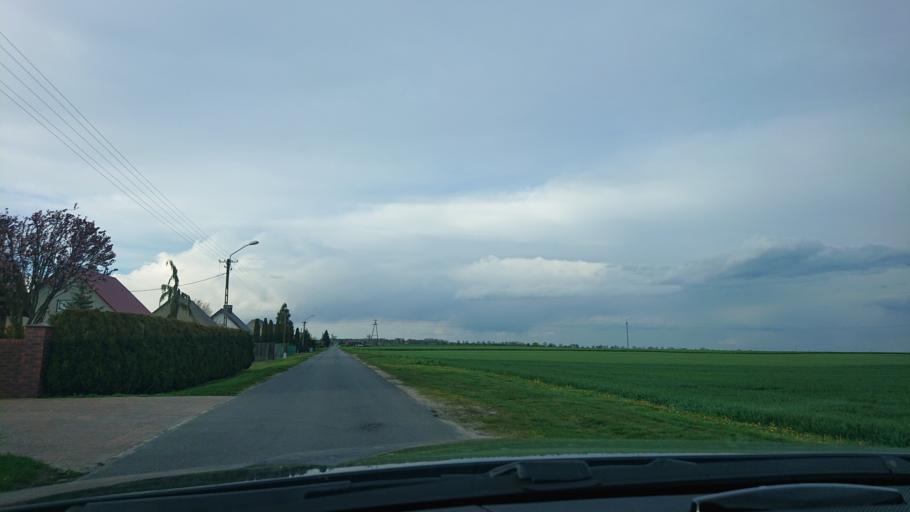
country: PL
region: Greater Poland Voivodeship
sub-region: Powiat gnieznienski
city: Lubowo
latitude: 52.5724
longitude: 17.4757
